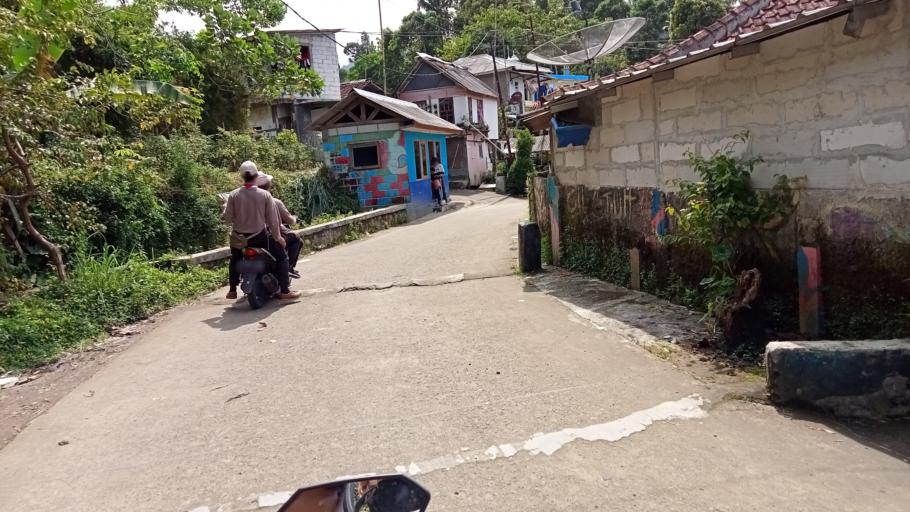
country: ID
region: West Java
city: Caringin
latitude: -6.6430
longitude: 106.9005
